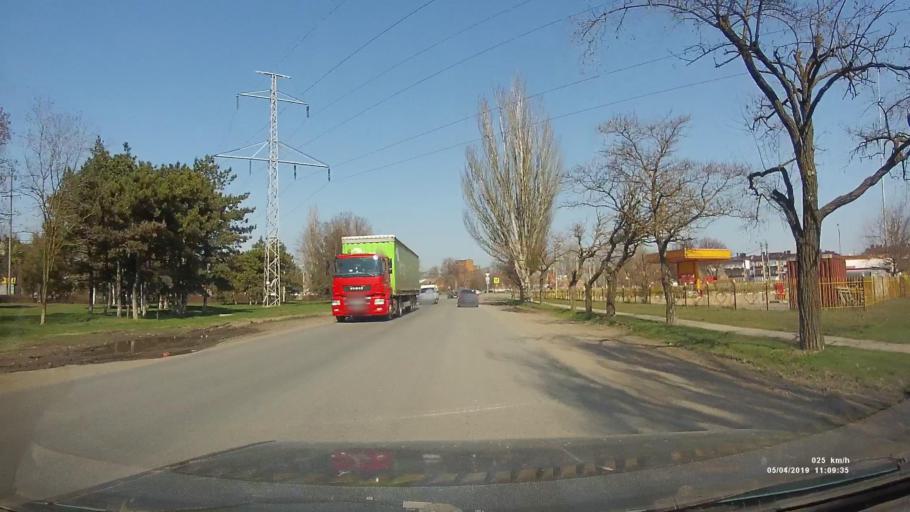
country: RU
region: Rostov
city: Azov
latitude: 47.0908
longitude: 39.4327
